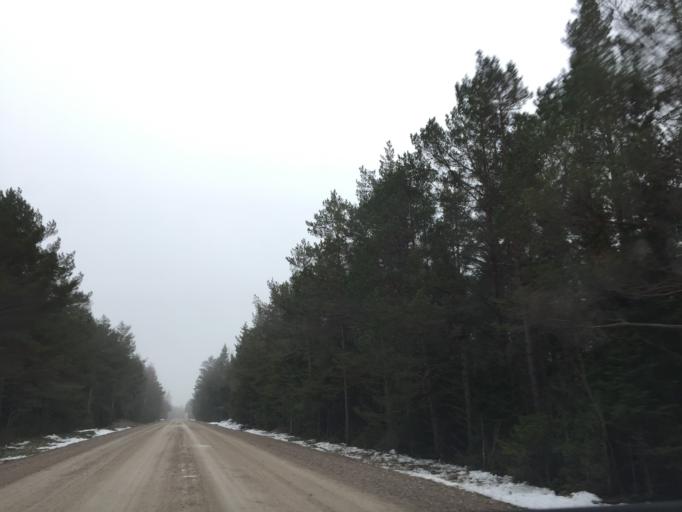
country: EE
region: Saare
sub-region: Kuressaare linn
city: Kuressaare
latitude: 58.4814
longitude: 21.9989
